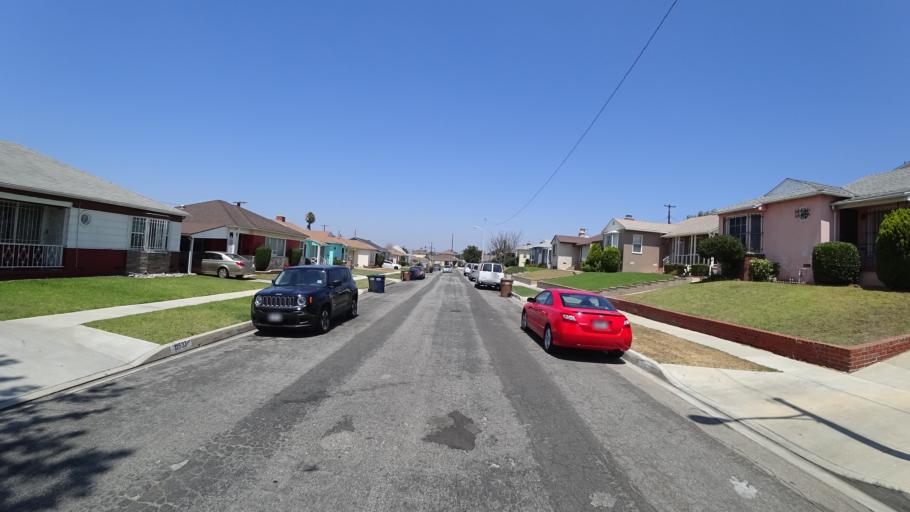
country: US
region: California
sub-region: Los Angeles County
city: West Athens
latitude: 33.9289
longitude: -118.3125
